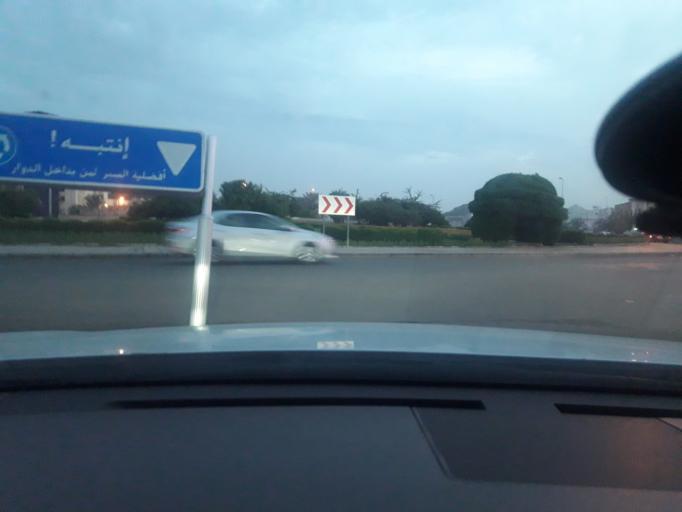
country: SA
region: Al Madinah al Munawwarah
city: Sultanah
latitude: 24.4933
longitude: 39.5854
